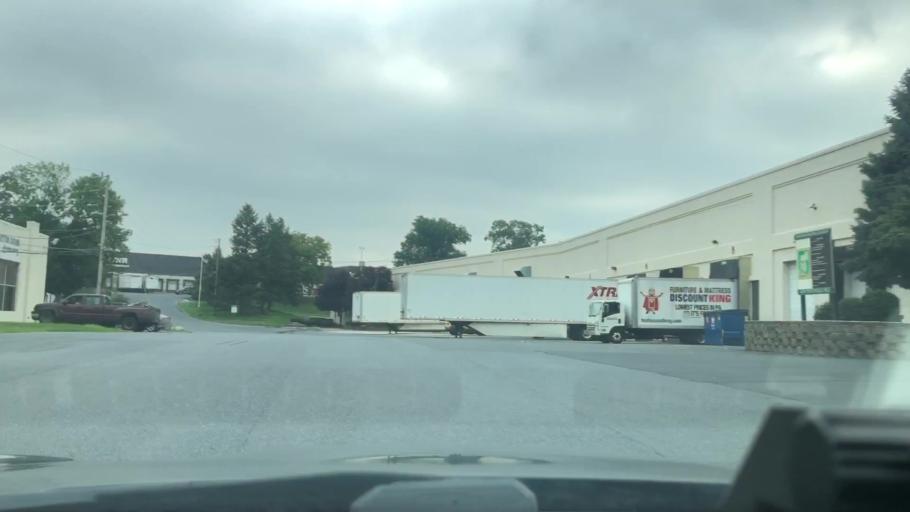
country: US
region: Pennsylvania
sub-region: Berks County
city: Muhlenberg Park
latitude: 40.3992
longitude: -75.9356
